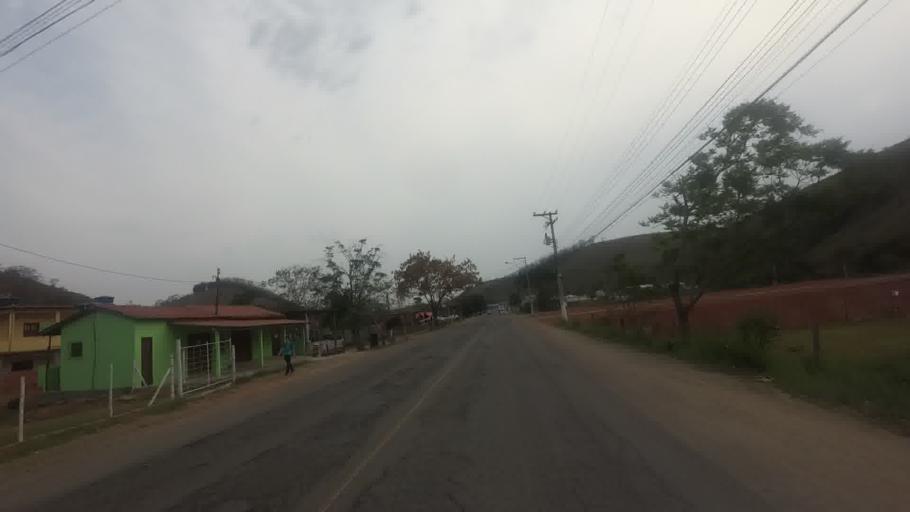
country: BR
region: Rio de Janeiro
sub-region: Santo Antonio De Padua
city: Santo Antonio de Padua
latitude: -21.5389
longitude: -42.1613
